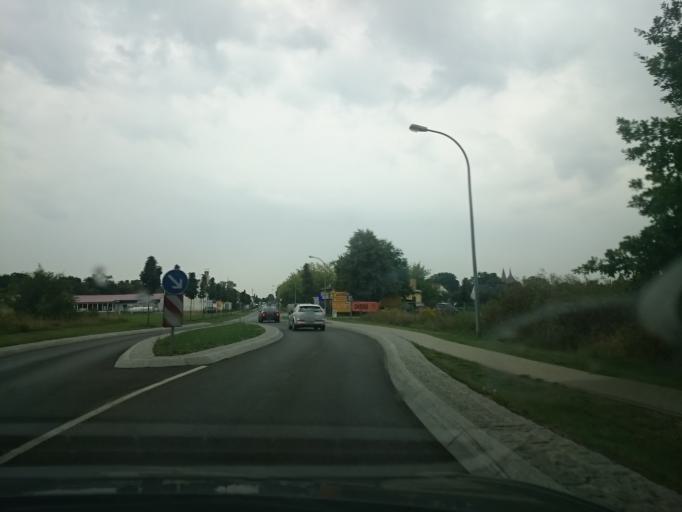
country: DE
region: Brandenburg
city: Gransee
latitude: 53.0100
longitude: 13.1701
